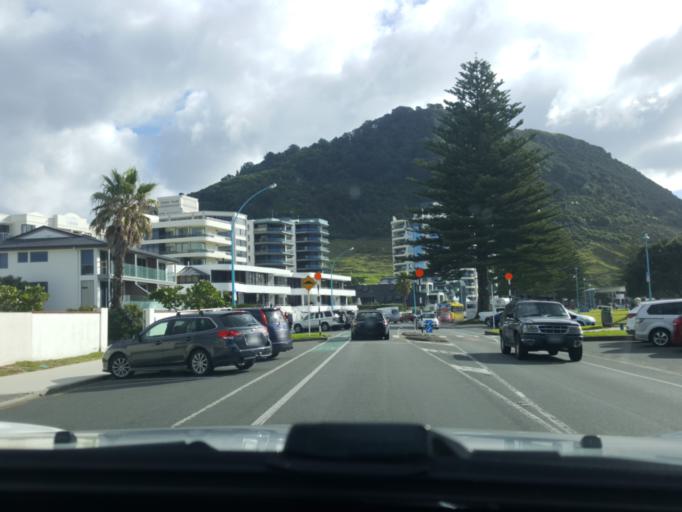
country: NZ
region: Bay of Plenty
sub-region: Tauranga City
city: Tauranga
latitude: -37.6328
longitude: 176.1803
